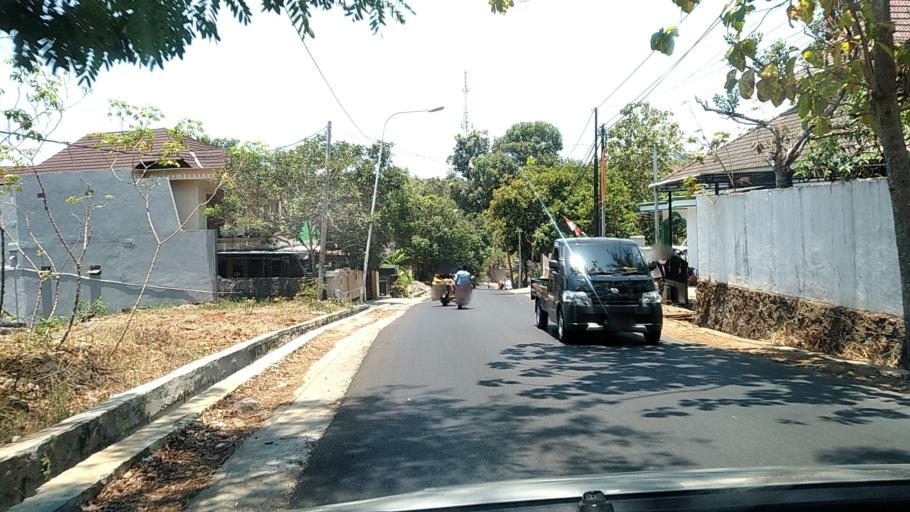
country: ID
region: Central Java
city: Semarang
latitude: -7.0586
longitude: 110.3914
